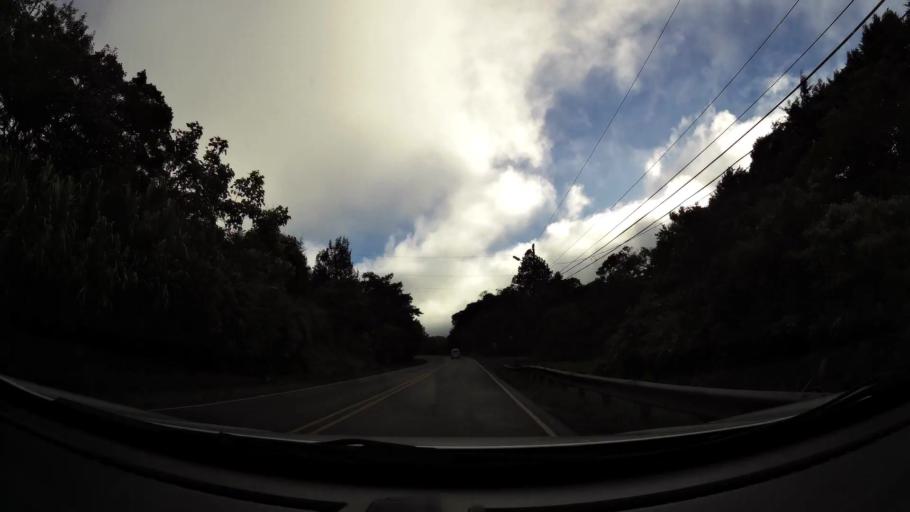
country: CR
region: Heredia
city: Angeles
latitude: 10.0305
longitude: -84.0056
